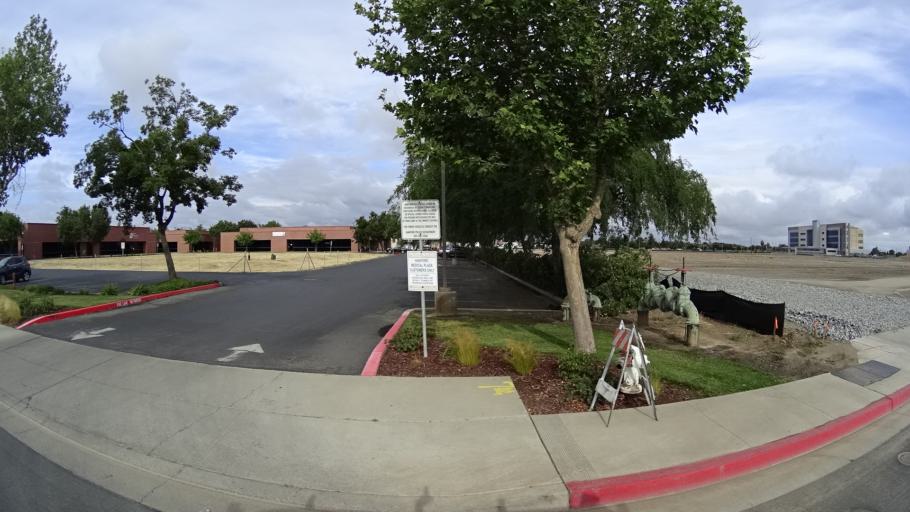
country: US
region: California
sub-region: Kings County
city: Hanford
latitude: 36.3305
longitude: -119.6685
